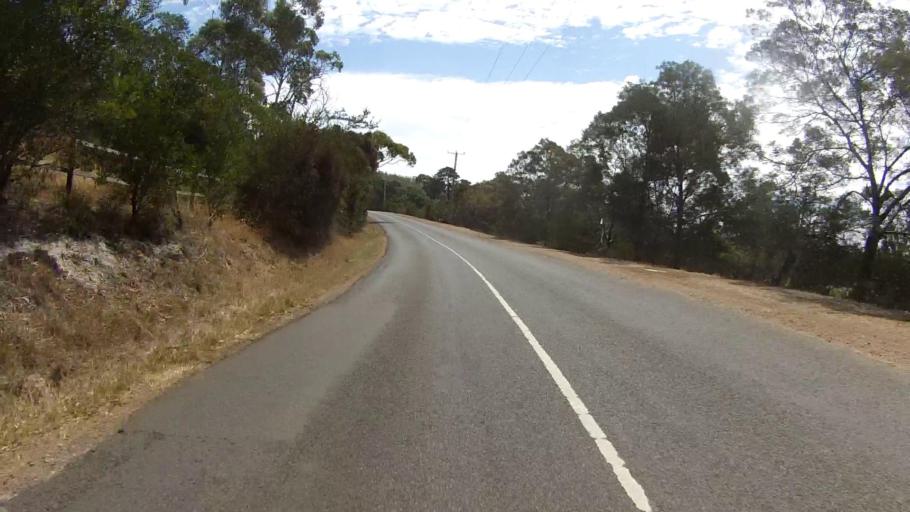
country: AU
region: Tasmania
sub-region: Clarence
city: Sandford
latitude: -42.9673
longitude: 147.5059
